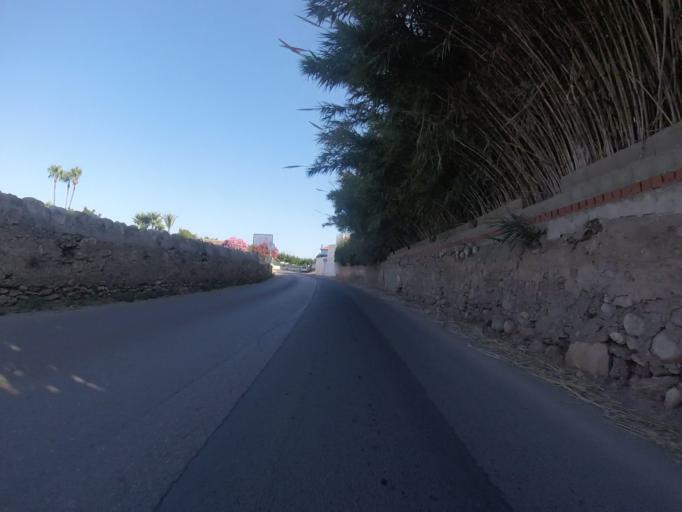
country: ES
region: Valencia
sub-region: Provincia de Castello
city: Benicarlo
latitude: 40.4013
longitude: 0.4147
